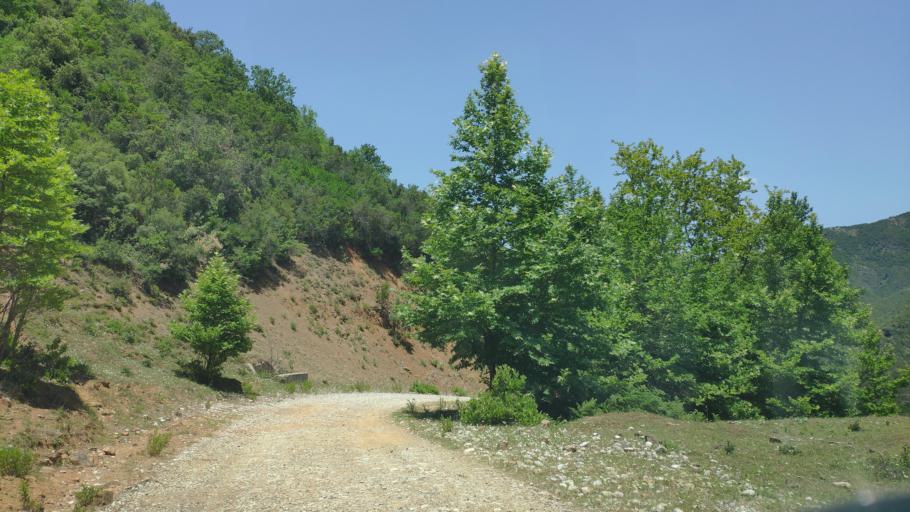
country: GR
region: Thessaly
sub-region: Nomos Kardhitsas
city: Anthiro
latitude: 39.1764
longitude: 21.3701
